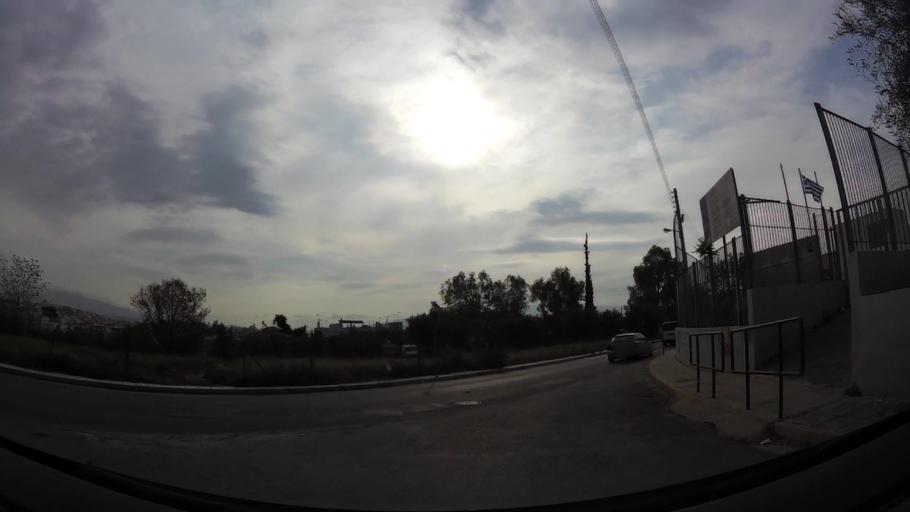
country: GR
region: Attica
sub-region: Nomarchia Athinas
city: Kamateron
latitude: 38.0564
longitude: 23.7061
